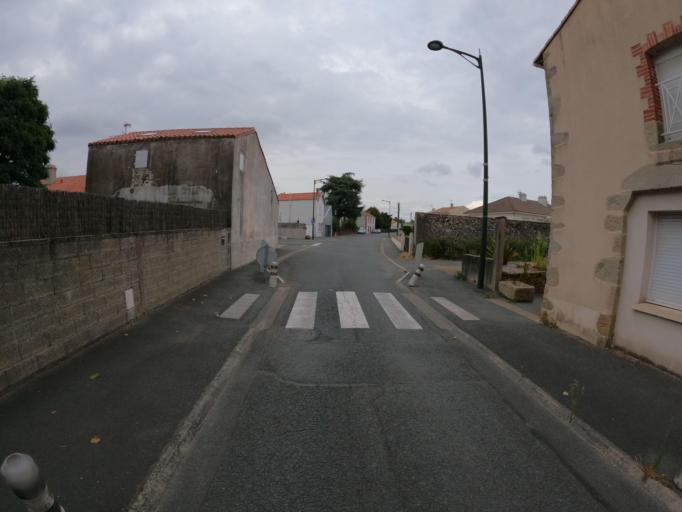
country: FR
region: Pays de la Loire
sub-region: Departement de Maine-et-Loire
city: Le Longeron
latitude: 47.0195
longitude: -1.0588
